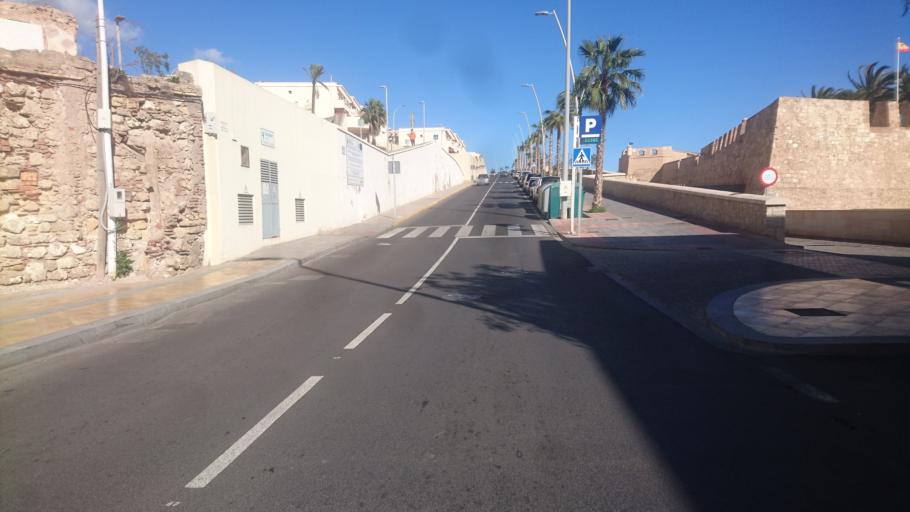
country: ES
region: Melilla
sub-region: Melilla
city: Melilla
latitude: 35.2938
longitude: -2.9374
